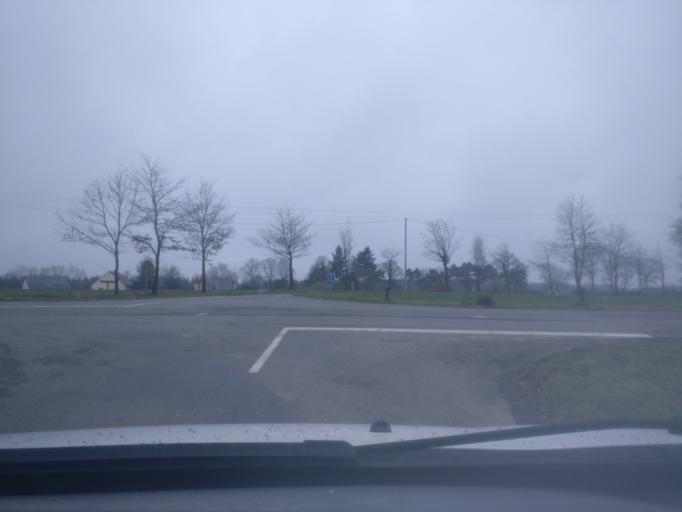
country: FR
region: Brittany
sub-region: Departement d'Ille-et-Vilaine
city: Chasne-sur-Illet
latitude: 48.2904
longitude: -1.5837
